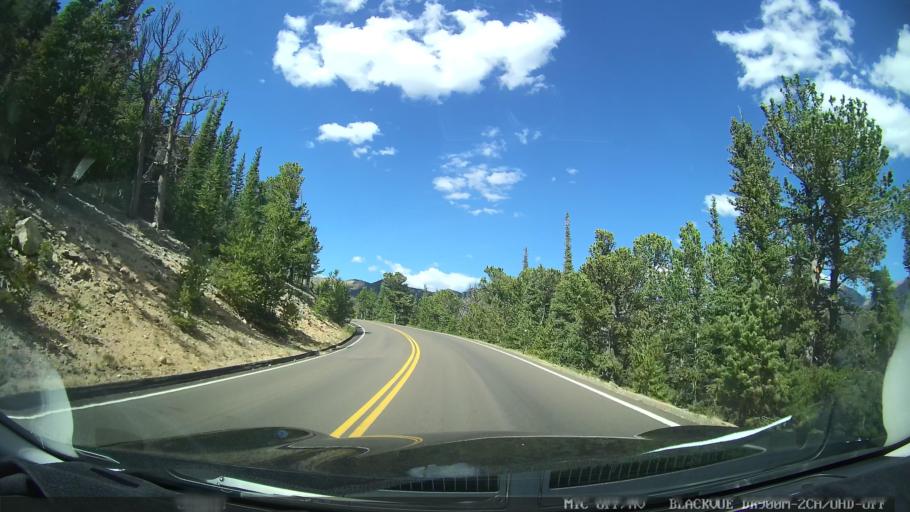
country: US
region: Colorado
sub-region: Larimer County
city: Estes Park
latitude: 40.3946
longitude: -105.6424
